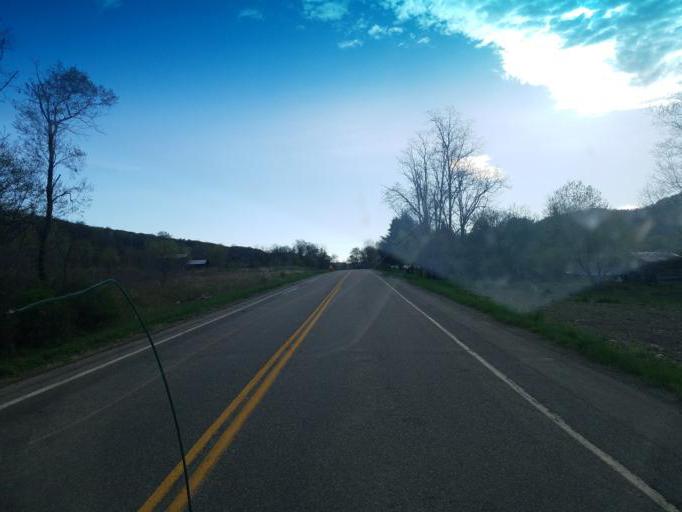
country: US
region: New York
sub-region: Allegany County
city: Andover
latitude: 42.0184
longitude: -77.8266
